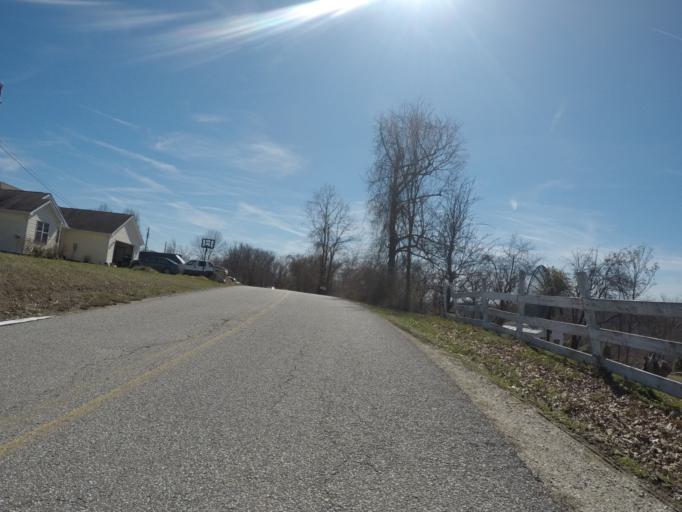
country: US
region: West Virginia
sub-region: Cabell County
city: Huntington
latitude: 38.4522
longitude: -82.4928
